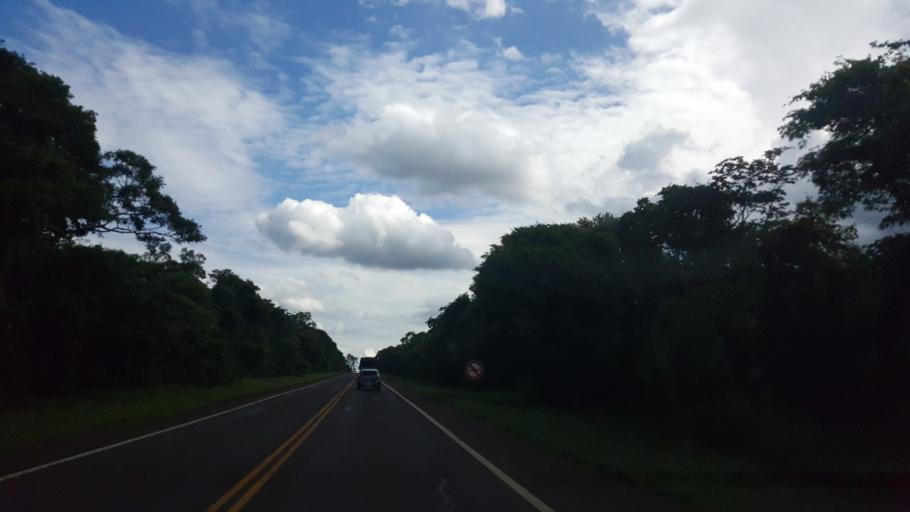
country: AR
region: Misiones
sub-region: Departamento de Iguazu
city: Puerto Iguazu
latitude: -25.6925
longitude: -54.5148
